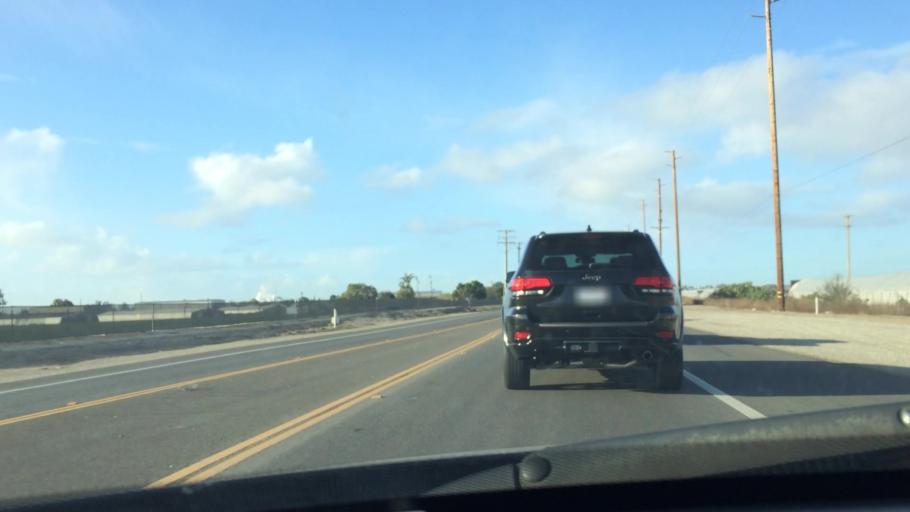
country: US
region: California
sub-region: Ventura County
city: El Rio
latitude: 34.2373
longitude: -119.1276
